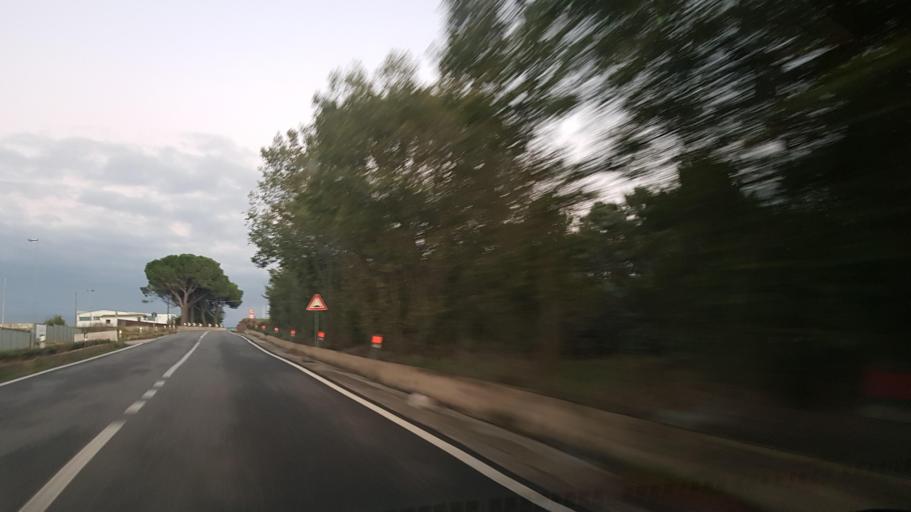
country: IT
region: Basilicate
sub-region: Provincia di Matera
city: Matera
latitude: 40.6781
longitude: 16.6550
